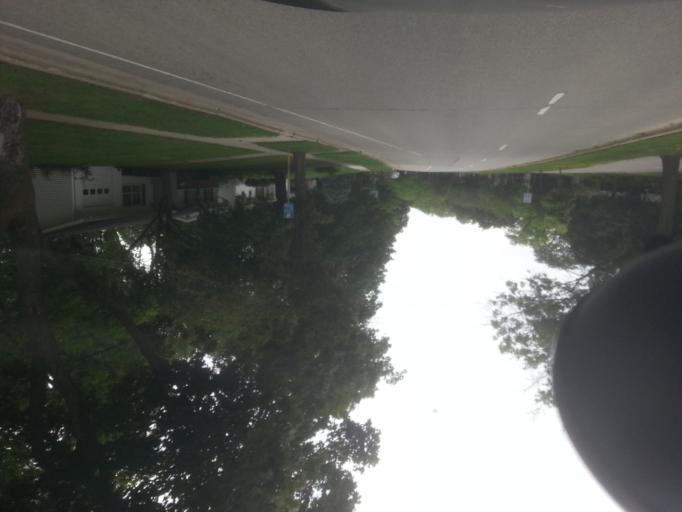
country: US
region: Wisconsin
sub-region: Dane County
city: Shorewood Hills
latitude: 43.0640
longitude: -89.4715
